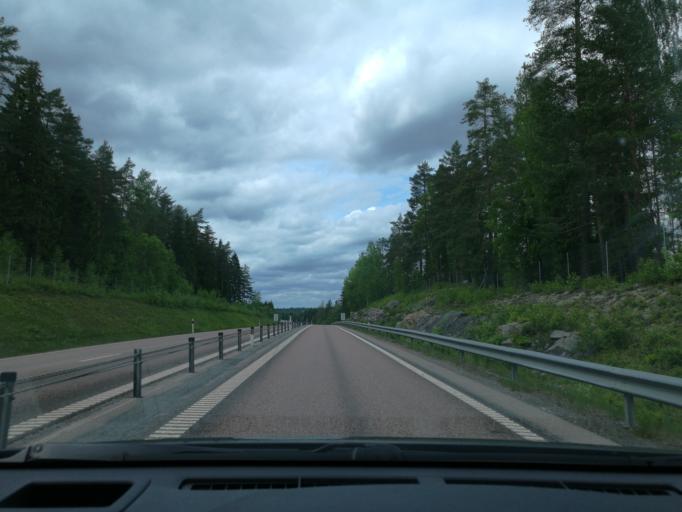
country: SE
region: Vaestmanland
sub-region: Fagersta Kommun
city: Fagersta
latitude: 59.9687
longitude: 15.8341
